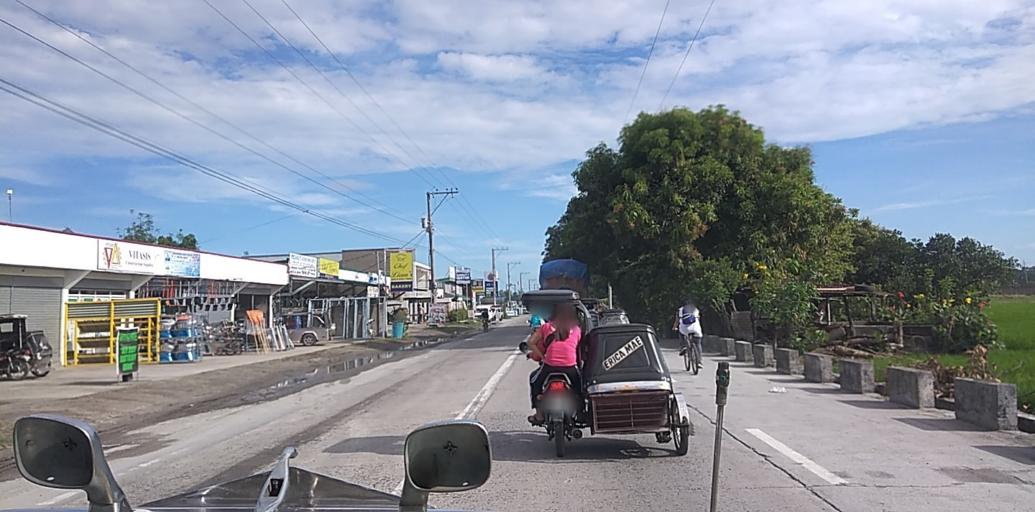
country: PH
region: Central Luzon
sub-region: Province of Pampanga
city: Bulaon
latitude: 15.1009
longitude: 120.6580
